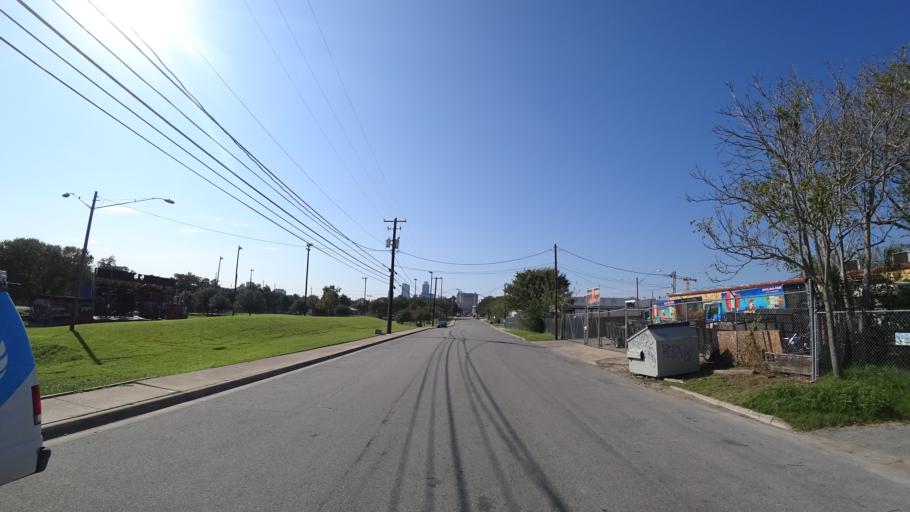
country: US
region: Texas
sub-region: Travis County
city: Austin
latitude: 30.2589
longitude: -97.7209
